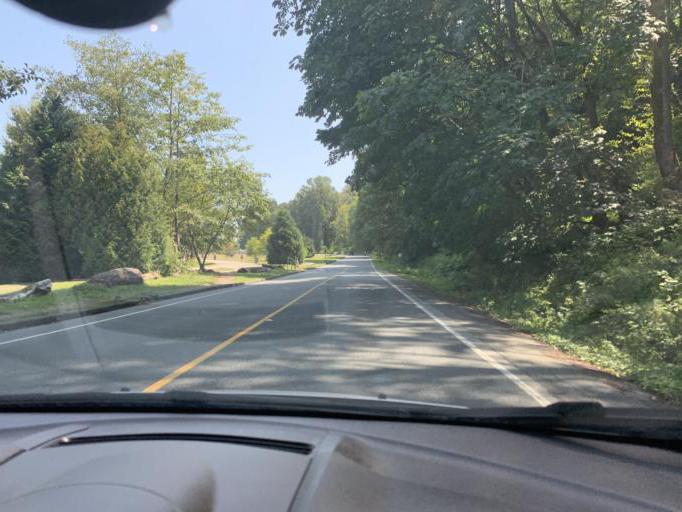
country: CA
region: British Columbia
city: West End
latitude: 49.2788
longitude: -123.2369
